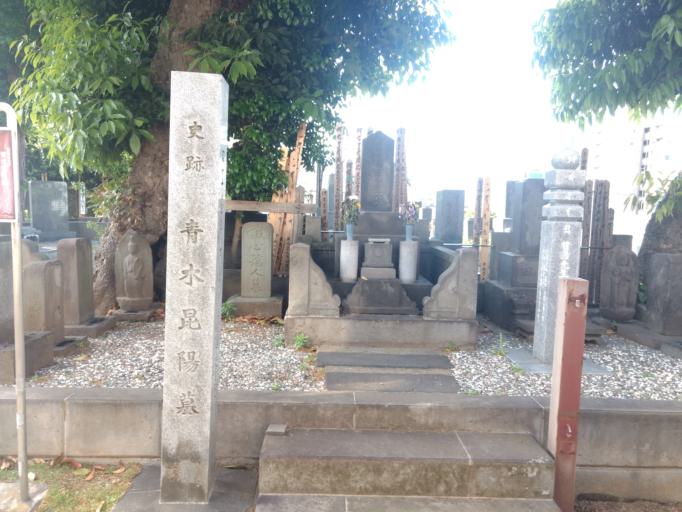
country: JP
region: Tokyo
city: Tokyo
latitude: 35.6297
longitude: 139.7093
